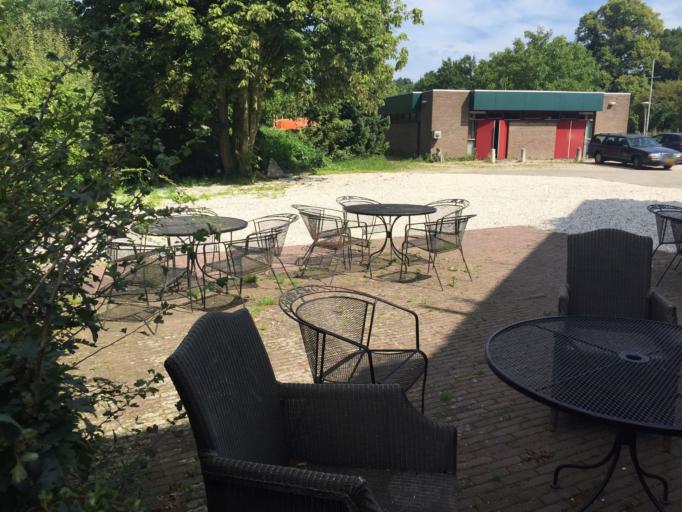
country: NL
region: Utrecht
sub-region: Gemeente Nieuwegein
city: Nieuwegein
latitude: 52.0377
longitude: 5.0999
